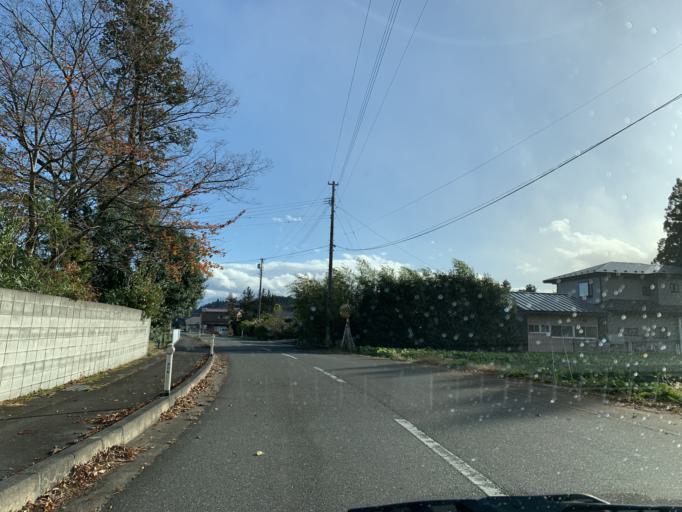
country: JP
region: Iwate
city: Mizusawa
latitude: 39.0256
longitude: 141.0776
